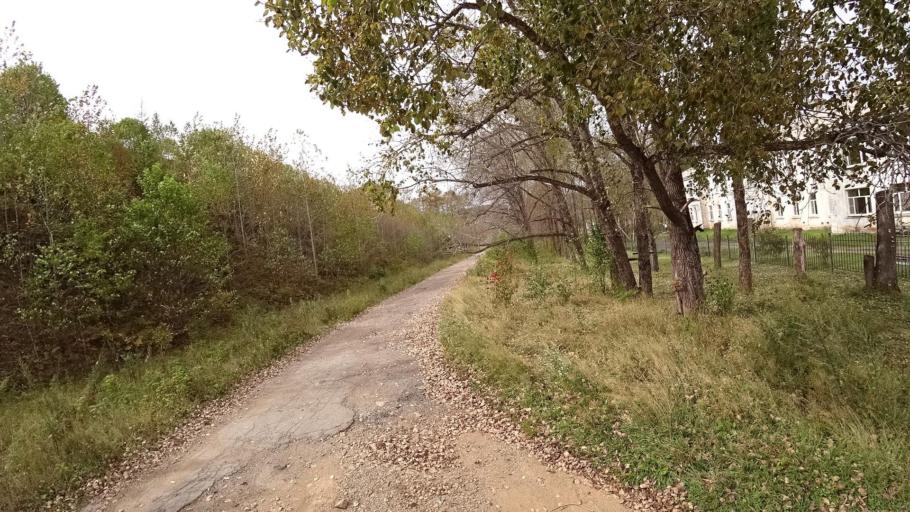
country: RU
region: Jewish Autonomous Oblast
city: Khingansk
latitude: 49.1239
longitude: 131.1989
